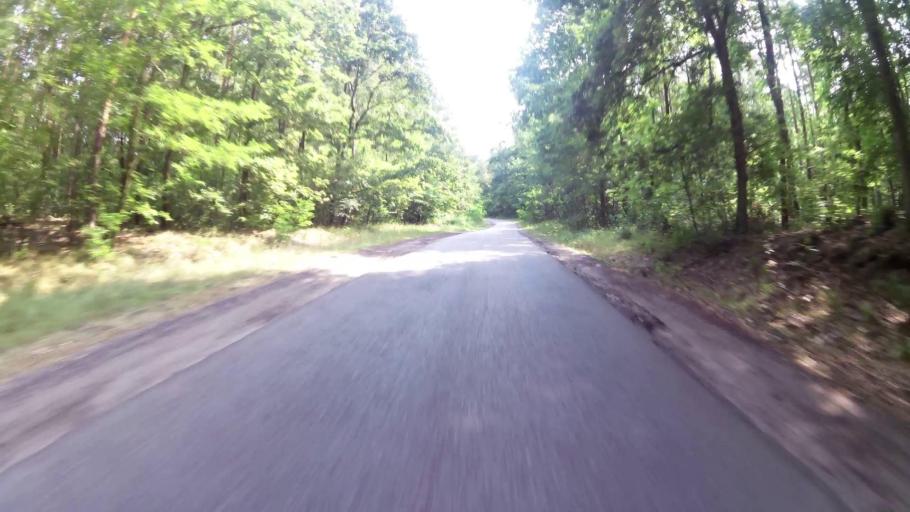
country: PL
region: West Pomeranian Voivodeship
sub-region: Powiat gryfinski
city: Chojna
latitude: 52.9109
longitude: 14.4685
